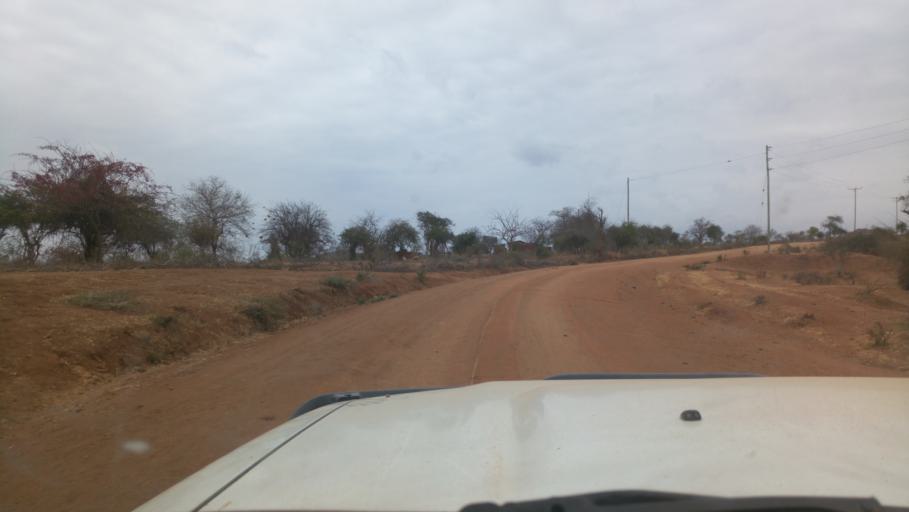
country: KE
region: Makueni
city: Makueni
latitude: -2.0073
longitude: 38.1125
